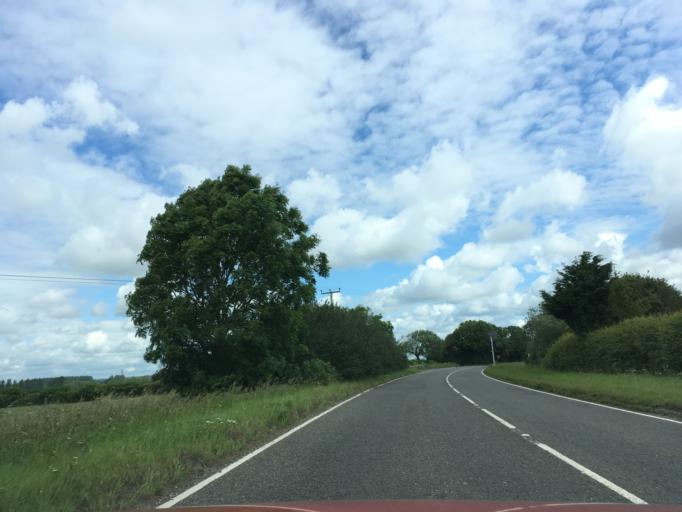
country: GB
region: England
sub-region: Gloucestershire
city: Lechlade
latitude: 51.6706
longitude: -1.7064
